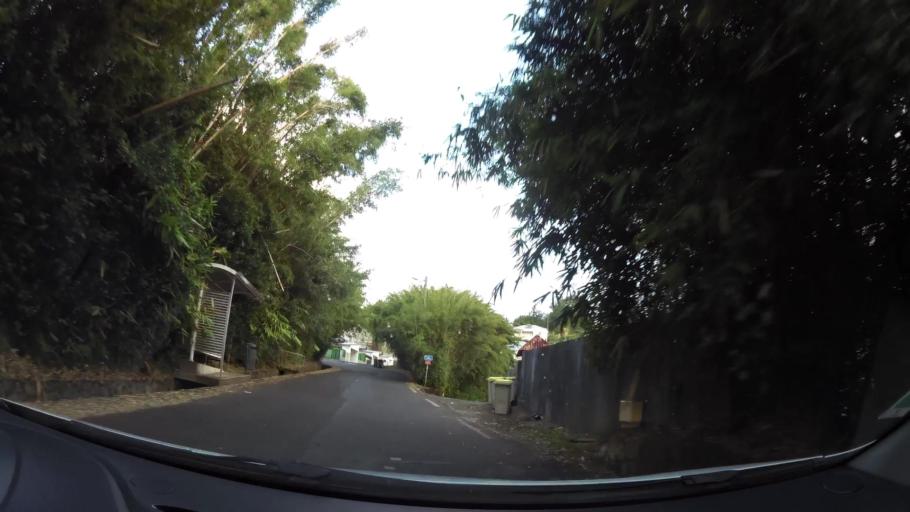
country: RE
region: Reunion
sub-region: Reunion
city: Saint-Denis
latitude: -20.9196
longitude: 55.4375
